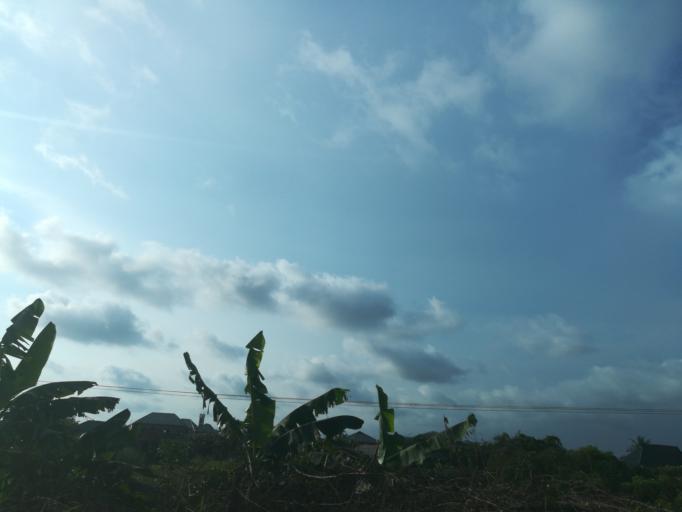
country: NG
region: Ogun
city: Ado Odo
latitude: 6.4800
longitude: 3.0244
